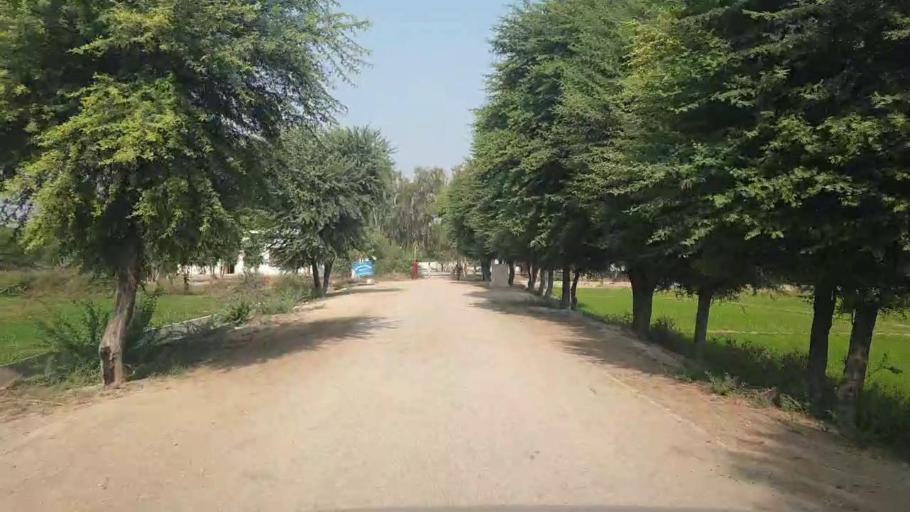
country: PK
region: Sindh
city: Umarkot
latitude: 25.3766
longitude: 69.7259
